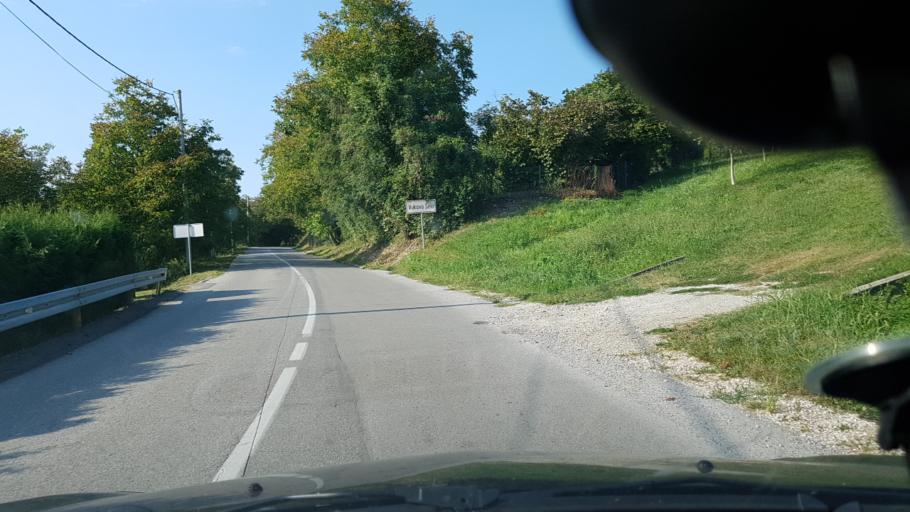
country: HR
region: Zagrebacka
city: Bregana
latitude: 45.8962
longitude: 15.6844
